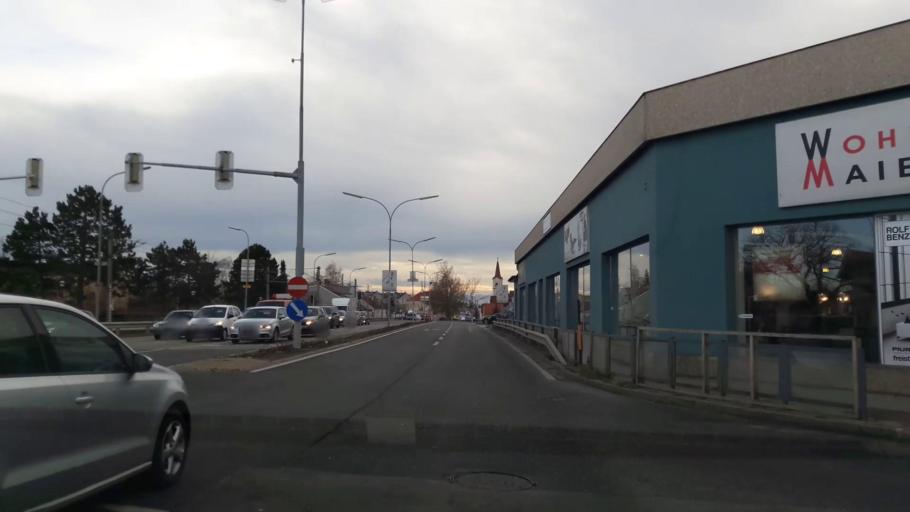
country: AT
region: Lower Austria
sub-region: Politischer Bezirk Modling
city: Wiener Neudorf
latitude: 48.0869
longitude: 16.3137
